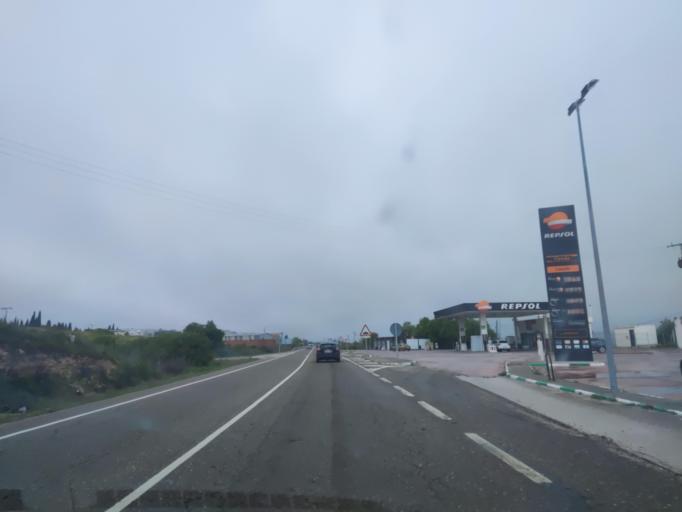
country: ES
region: Castille-La Mancha
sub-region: Province of Toledo
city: Bargas
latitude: 39.9466
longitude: -4.0158
